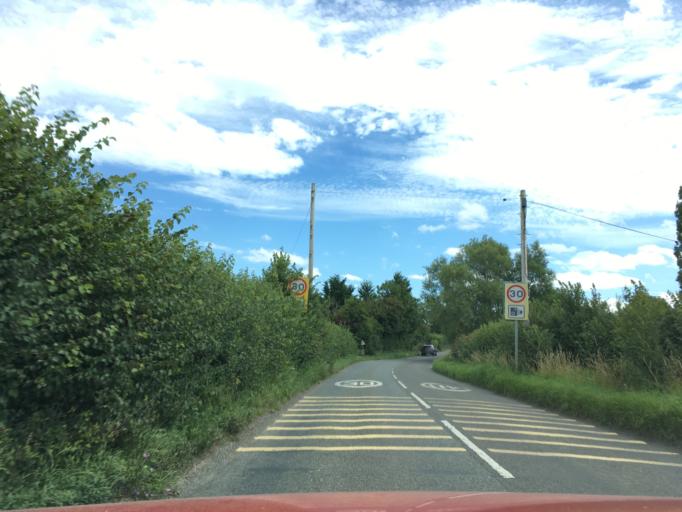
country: GB
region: England
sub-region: Somerset
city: Street
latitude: 51.1156
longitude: -2.7079
